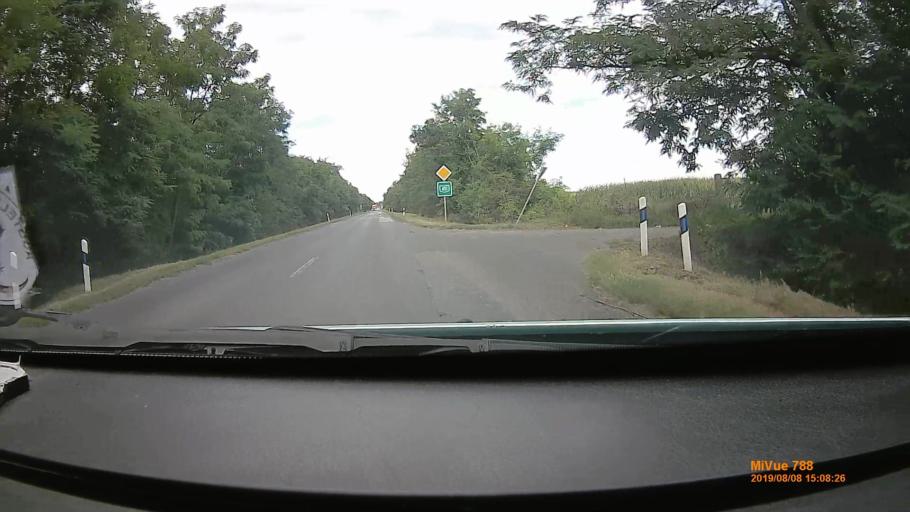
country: HU
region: Szabolcs-Szatmar-Bereg
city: Tunyogmatolcs
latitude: 47.9570
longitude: 22.4395
